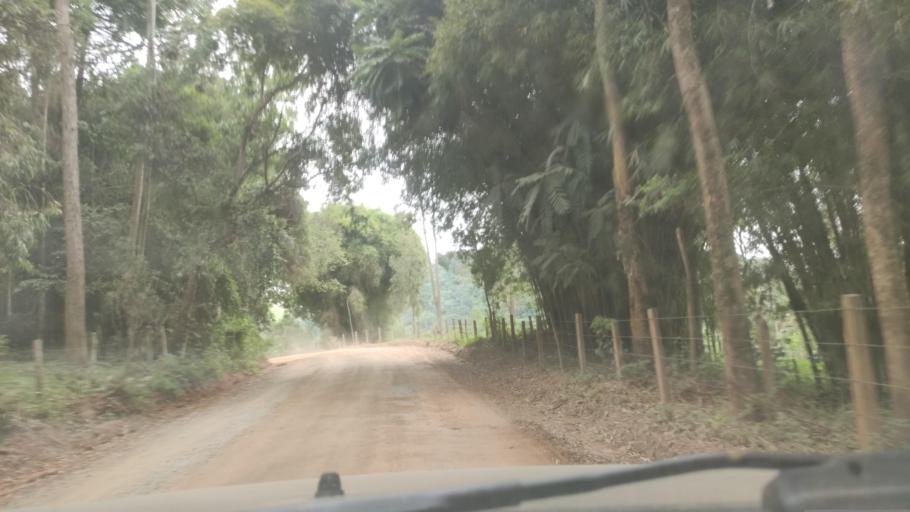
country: BR
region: Minas Gerais
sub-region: Paraisopolis
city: Paraisopolis
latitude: -22.6589
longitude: -45.8867
